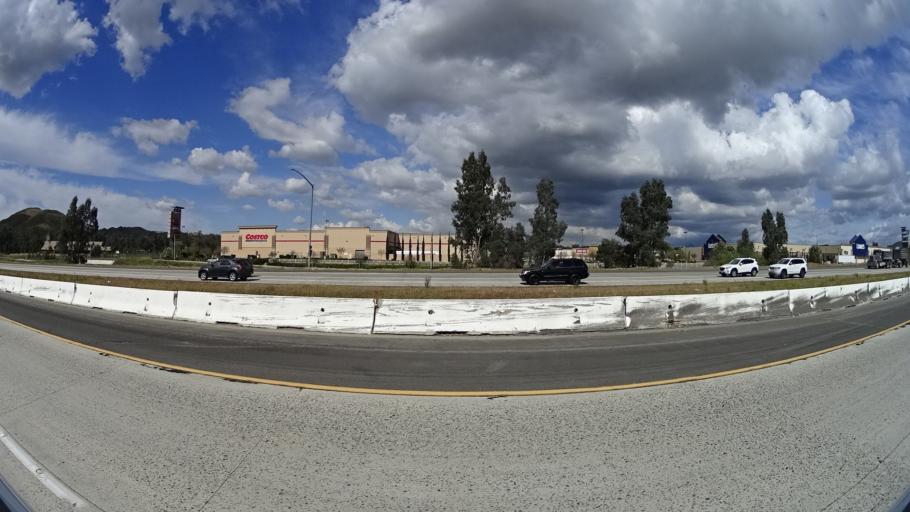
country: US
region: California
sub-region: Riverside County
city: Lake Elsinore
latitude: 33.6948
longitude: -117.3411
